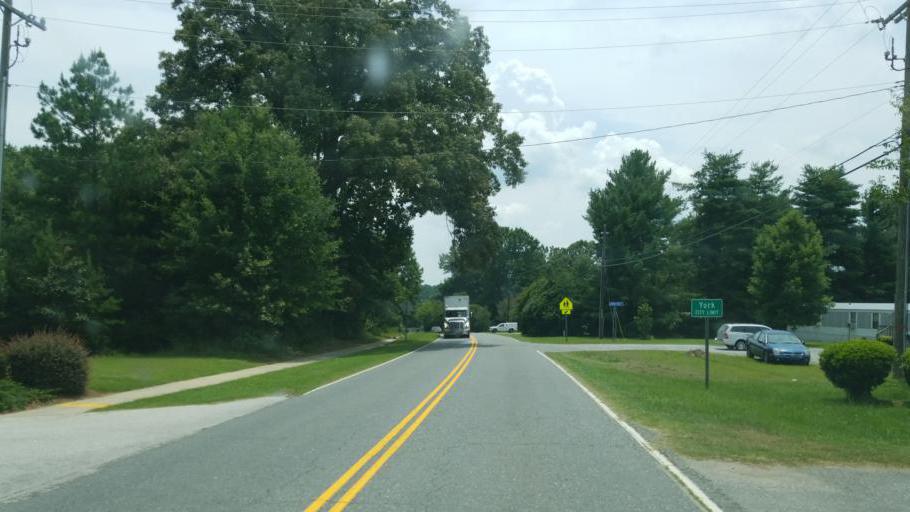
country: US
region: South Carolina
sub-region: York County
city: York
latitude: 35.0018
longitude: -81.2573
